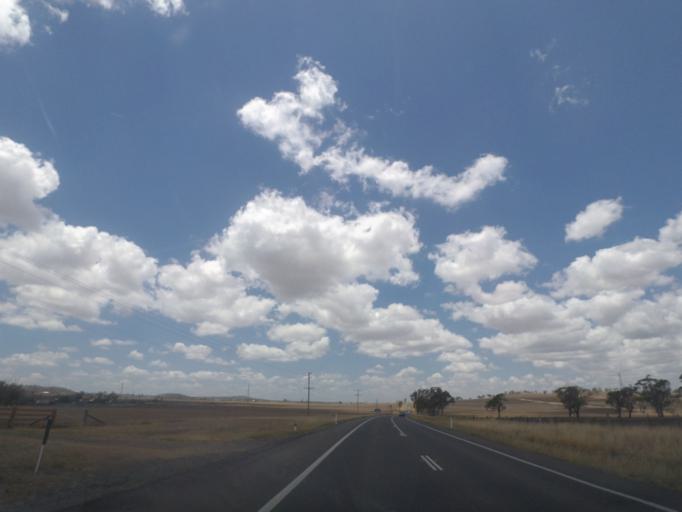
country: AU
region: Queensland
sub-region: Toowoomba
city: Top Camp
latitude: -27.7390
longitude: 151.9210
